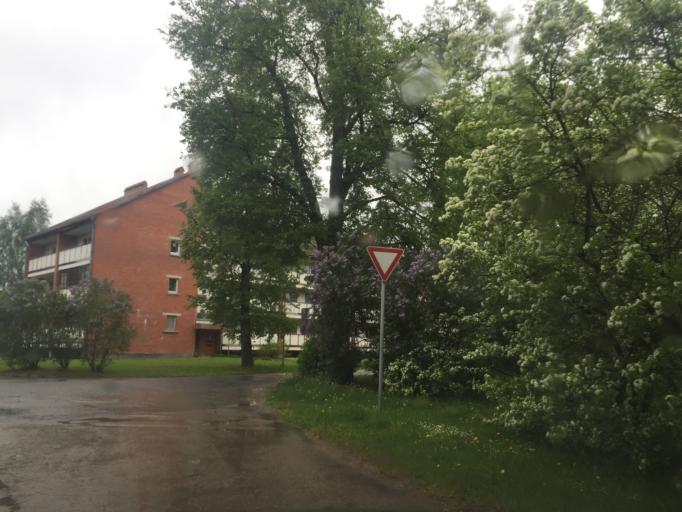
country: LV
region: Lielvarde
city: Lielvarde
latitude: 56.7125
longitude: 24.8342
